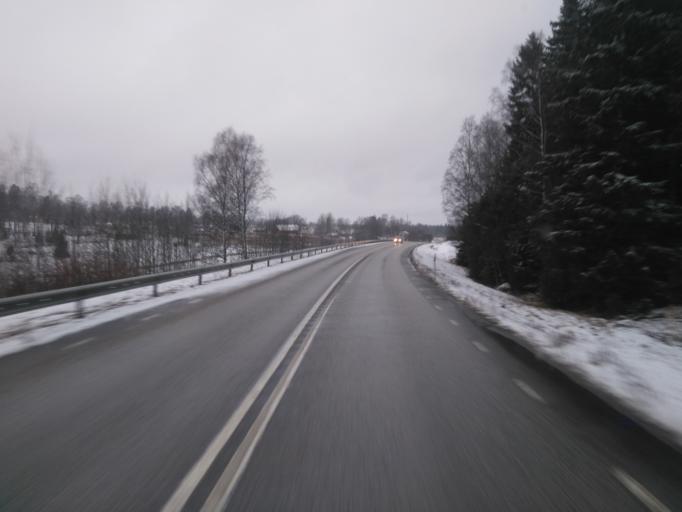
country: SE
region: Joenkoeping
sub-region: Eksjo Kommun
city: Eksjoe
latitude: 57.6507
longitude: 15.0300
